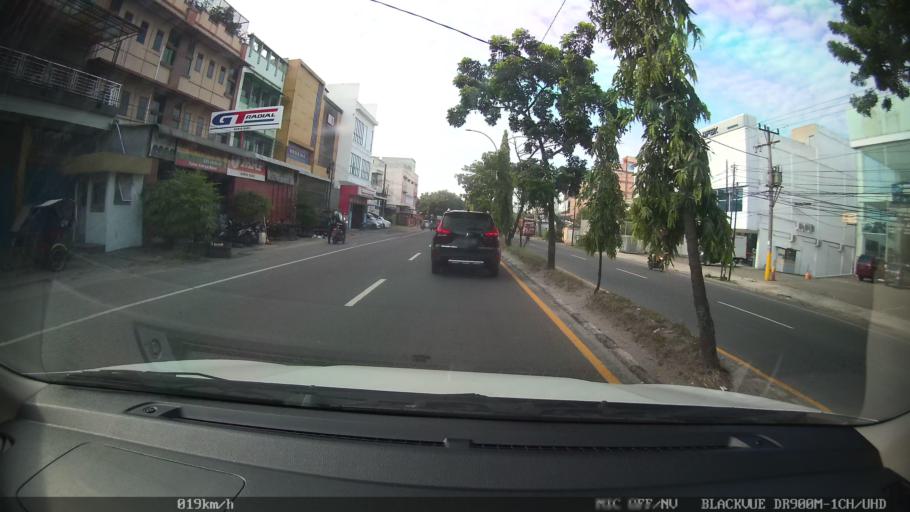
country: ID
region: North Sumatra
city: Medan
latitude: 3.6313
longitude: 98.6812
